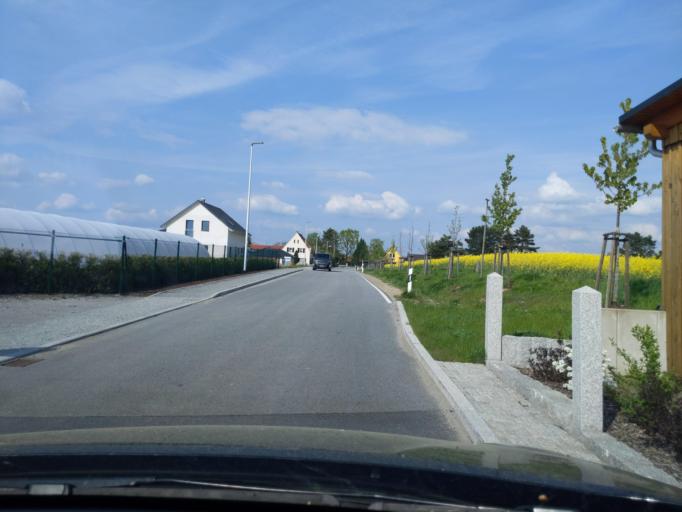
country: DE
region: Saxony
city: Kubschutz
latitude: 51.1732
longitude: 14.4902
